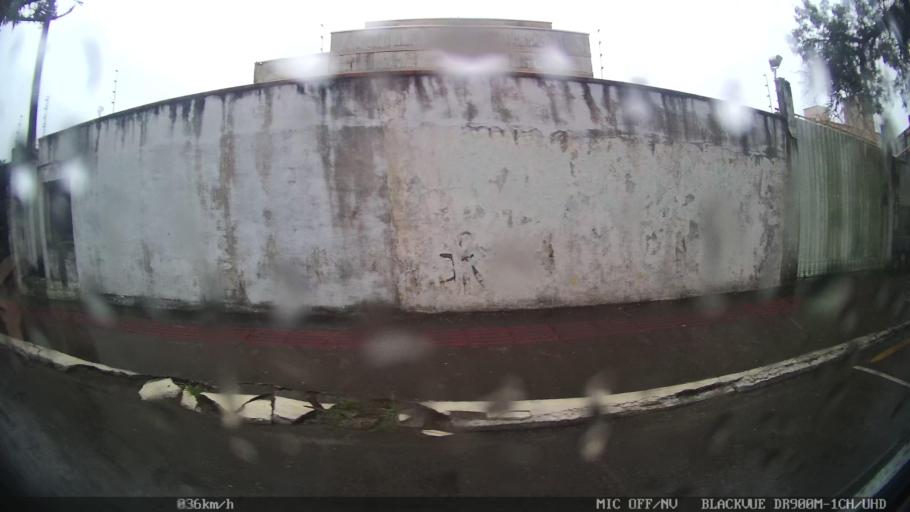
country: BR
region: Santa Catarina
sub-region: Balneario Camboriu
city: Balneario Camboriu
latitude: -27.0093
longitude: -48.6243
